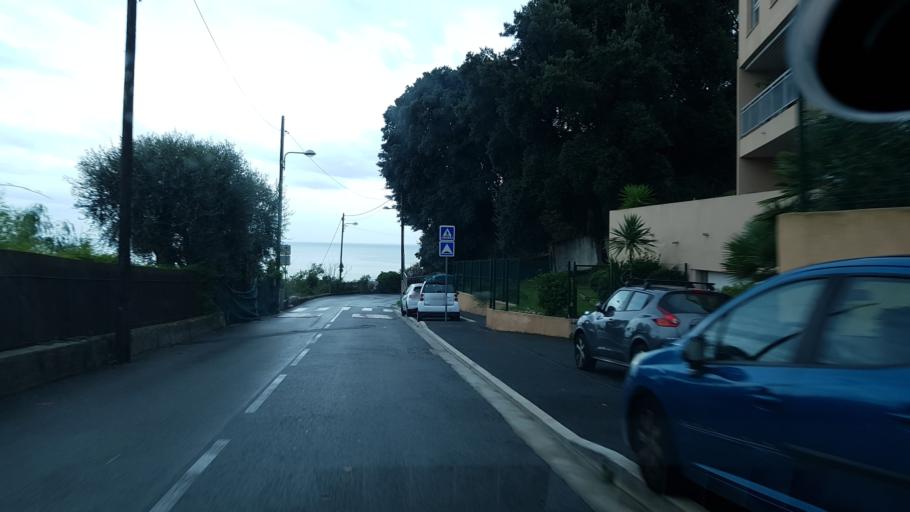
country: FR
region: Provence-Alpes-Cote d'Azur
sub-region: Departement des Alpes-Maritimes
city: Nice
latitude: 43.6965
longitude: 7.2392
